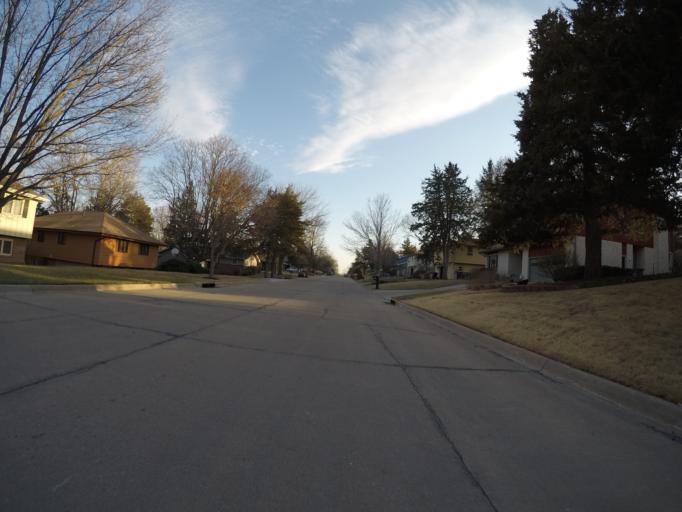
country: US
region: Kansas
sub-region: Riley County
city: Manhattan
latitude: 39.2028
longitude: -96.6243
